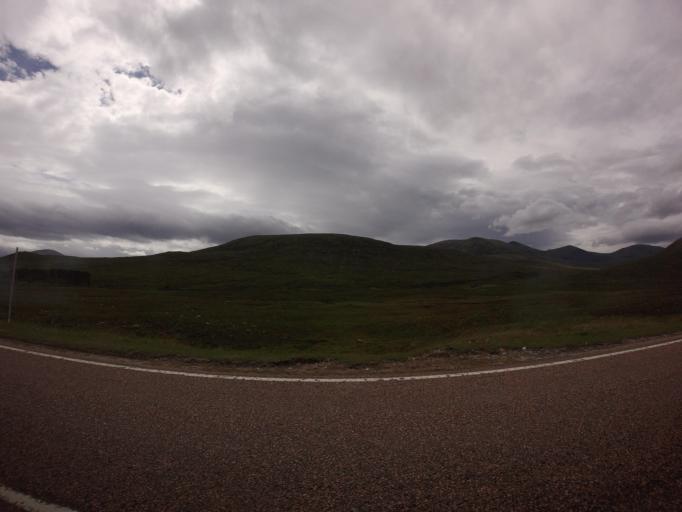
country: GB
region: Scotland
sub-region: Highland
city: Ullapool
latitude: 57.7363
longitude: -4.9456
